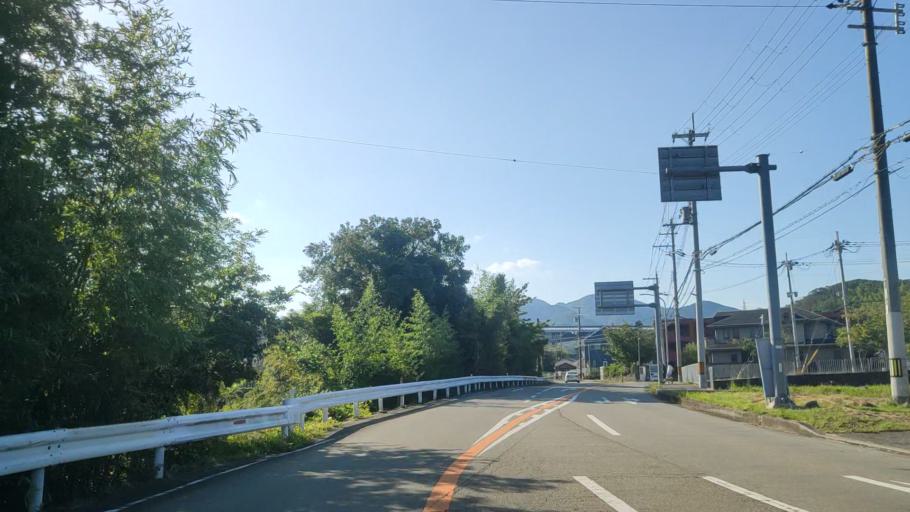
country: JP
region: Hyogo
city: Sandacho
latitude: 34.8205
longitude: 135.2468
